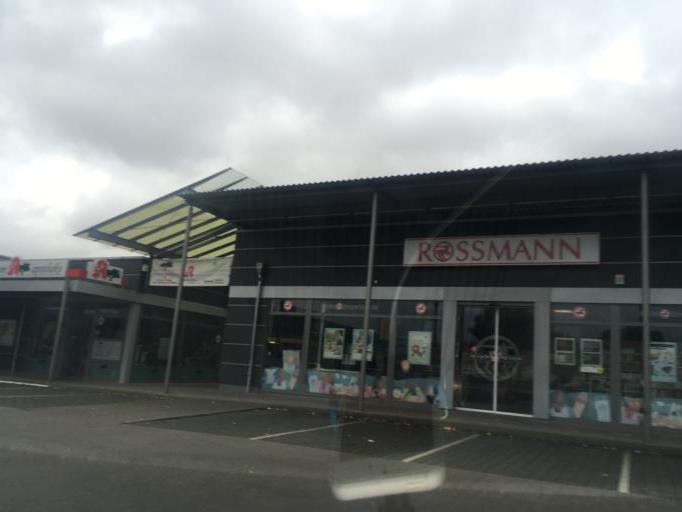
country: DE
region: Lower Saxony
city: Langenhagen
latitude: 52.4800
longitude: 9.7343
